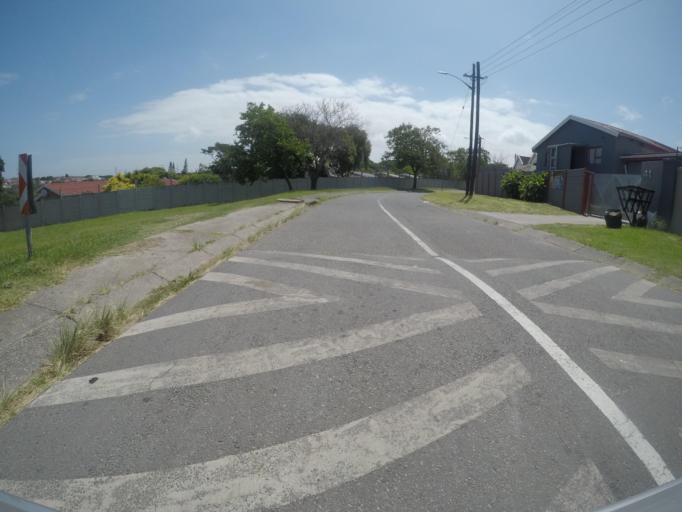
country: ZA
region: Eastern Cape
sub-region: Buffalo City Metropolitan Municipality
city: East London
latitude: -32.9723
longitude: 27.8622
